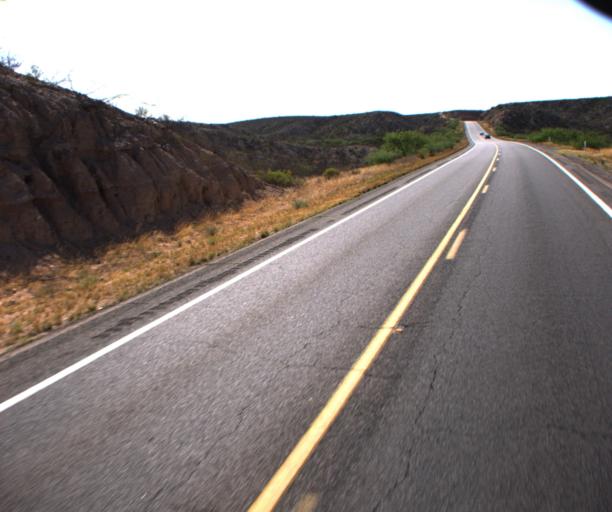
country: US
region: Arizona
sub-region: Cochise County
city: Saint David
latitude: 31.8212
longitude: -110.1728
